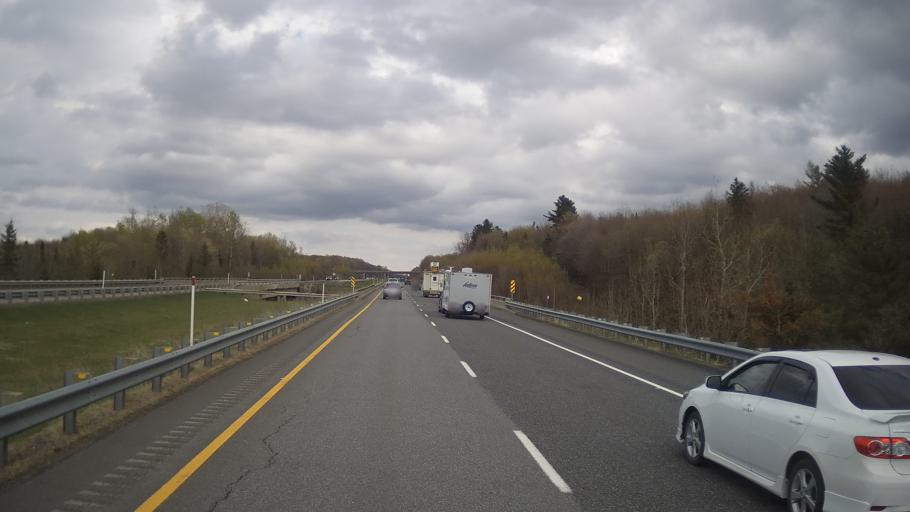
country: CA
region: Quebec
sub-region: Monteregie
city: Waterloo
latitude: 45.3022
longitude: -72.4300
